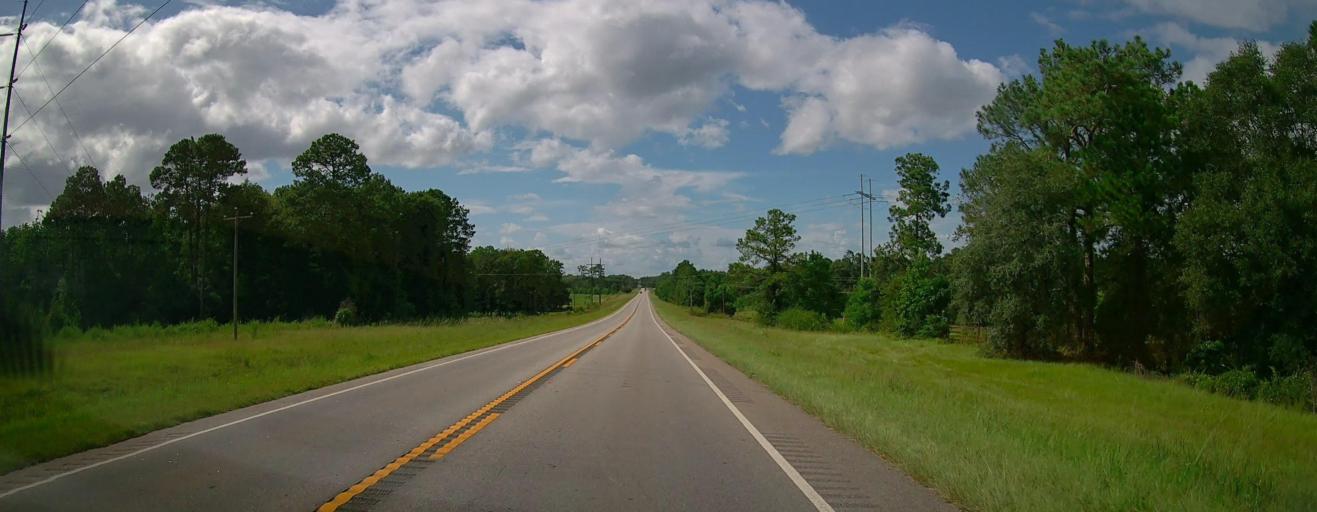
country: US
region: Georgia
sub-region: Coffee County
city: Douglas
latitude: 31.5313
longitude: -82.8800
